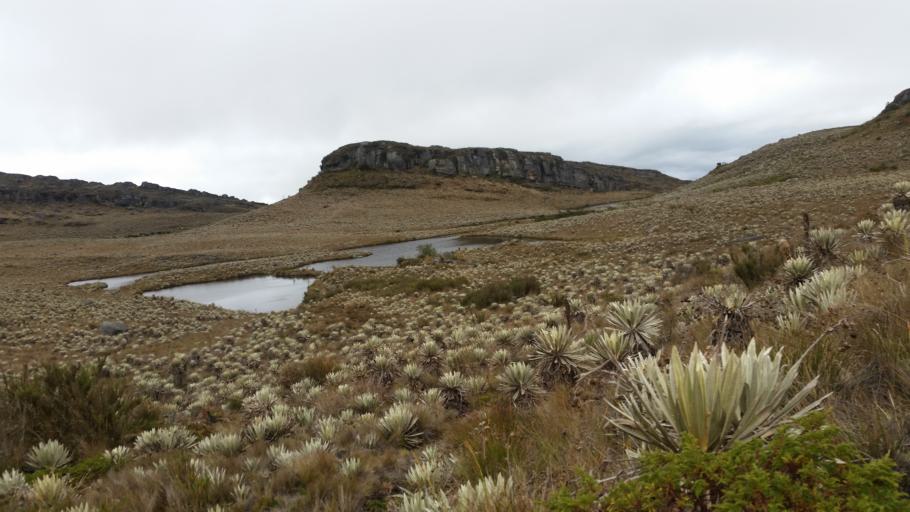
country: CO
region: Cundinamarca
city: Pasca
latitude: 4.3686
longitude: -74.2154
